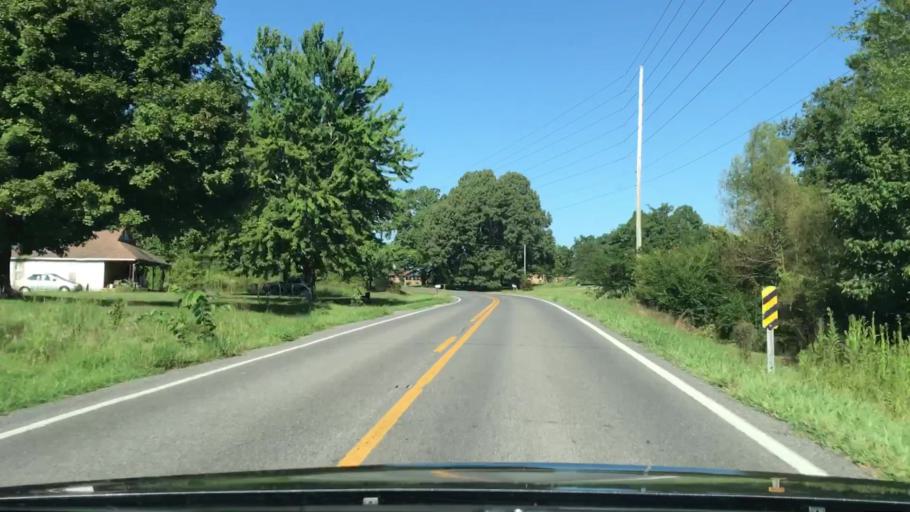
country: US
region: Kentucky
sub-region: Graves County
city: Mayfield
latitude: 36.7753
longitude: -88.4889
